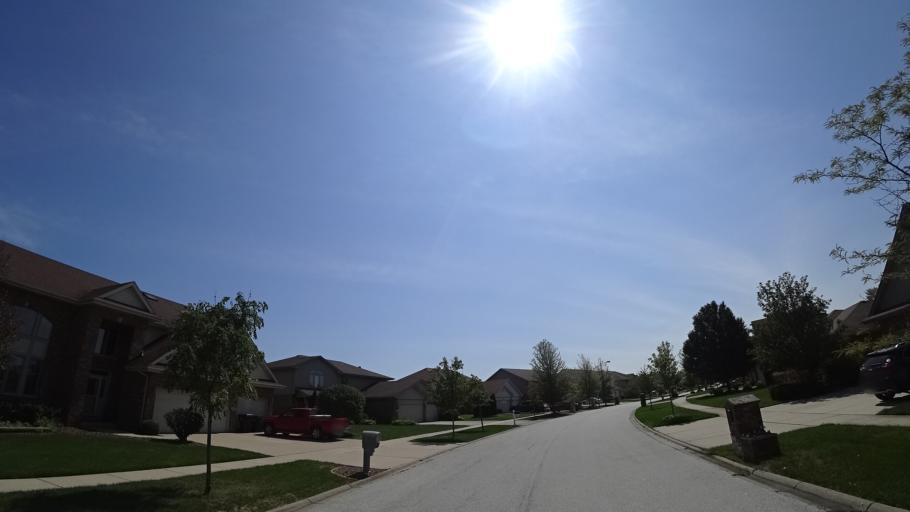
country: US
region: Illinois
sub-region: Cook County
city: Orland Hills
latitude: 41.5631
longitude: -87.8294
